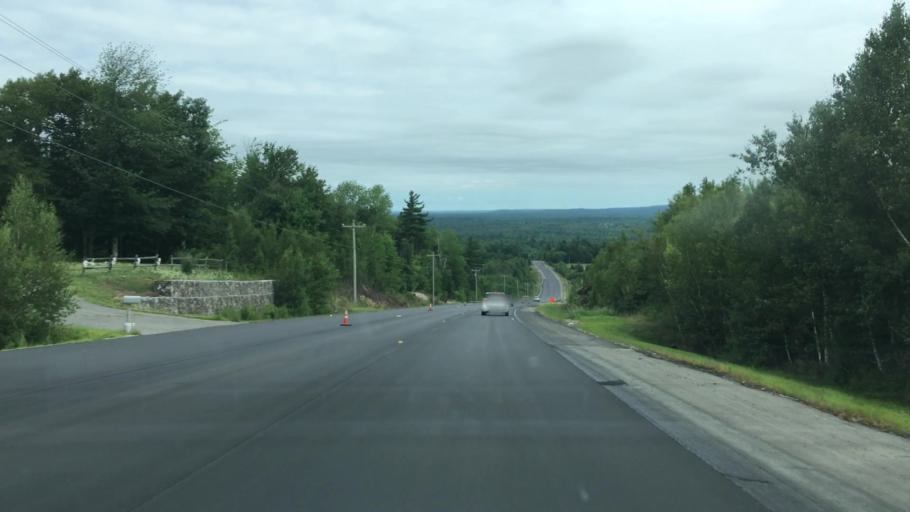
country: US
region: Maine
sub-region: Washington County
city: Machias
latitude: 44.9723
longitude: -67.6456
